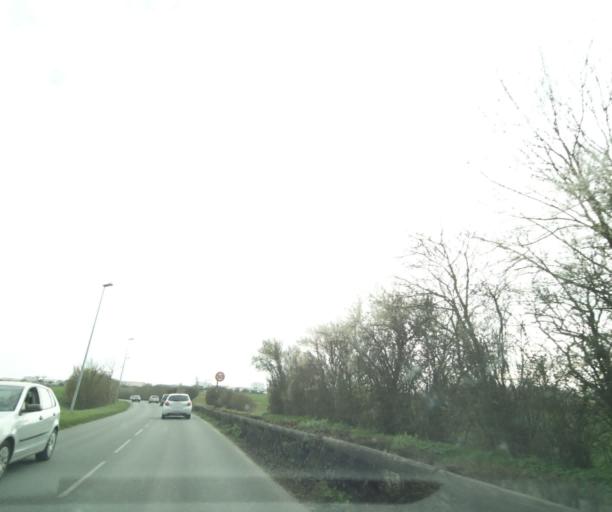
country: FR
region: Poitou-Charentes
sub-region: Departement de la Charente-Maritime
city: Lagord
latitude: 46.1795
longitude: -1.1675
